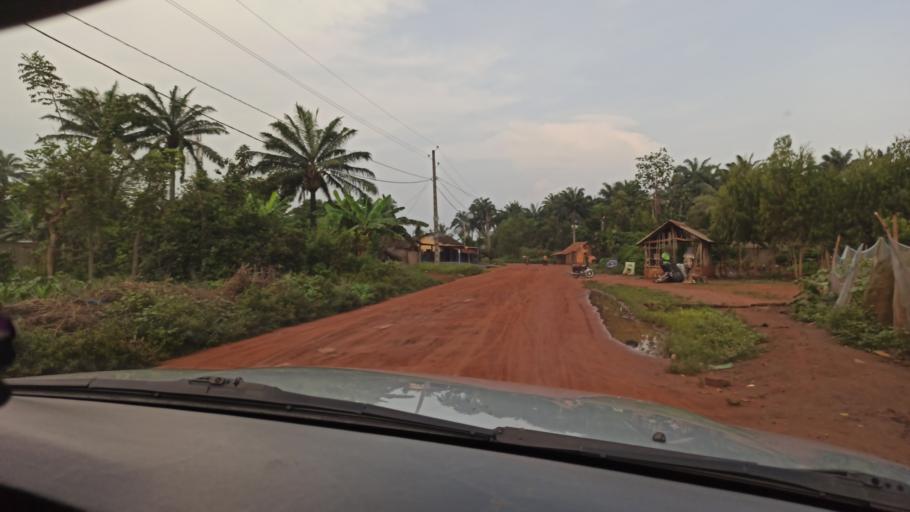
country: BJ
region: Queme
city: Porto-Novo
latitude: 6.4971
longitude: 2.6968
